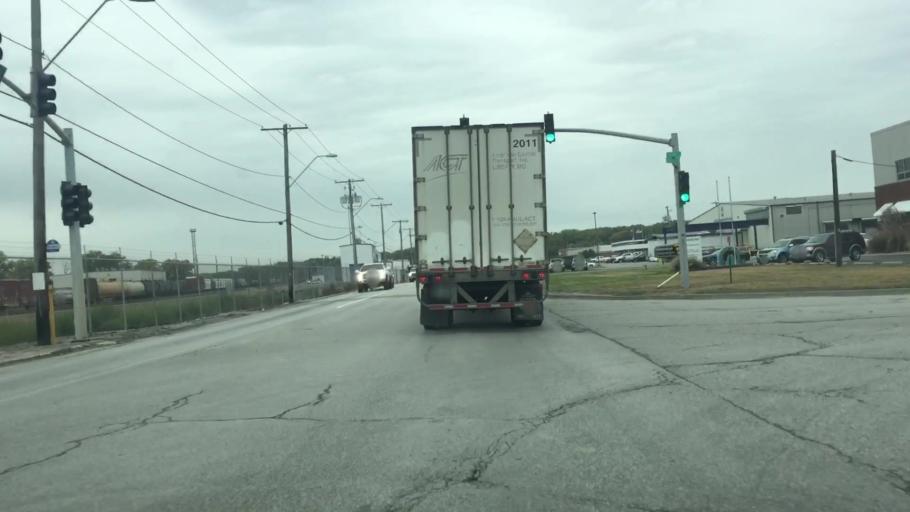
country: US
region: Missouri
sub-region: Clay County
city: North Kansas City
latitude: 39.1311
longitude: -94.5316
